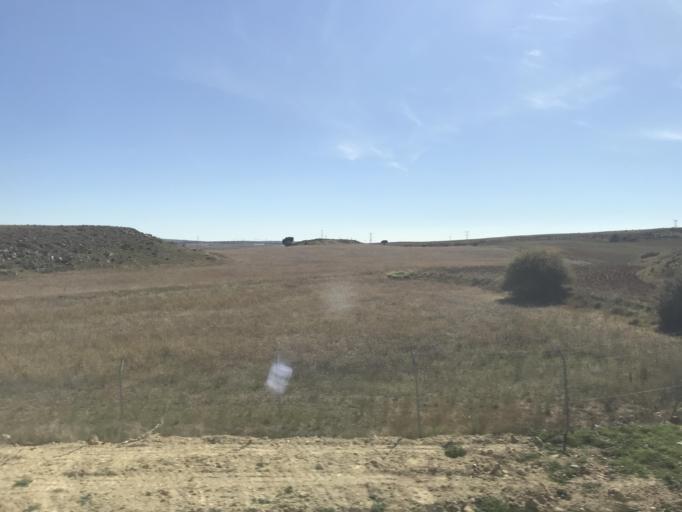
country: ES
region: Castille-La Mancha
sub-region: Provincia de Guadalajara
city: Anguita
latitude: 41.1119
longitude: -2.3612
